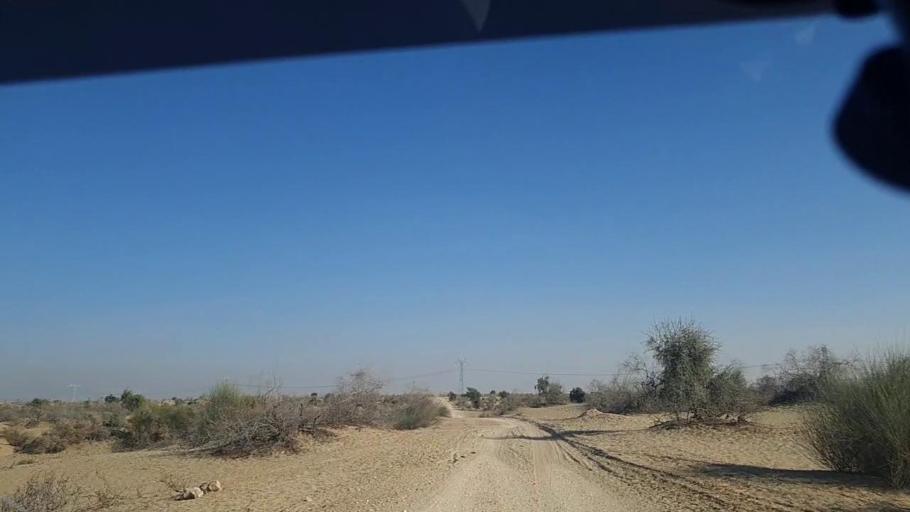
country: PK
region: Sindh
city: Khanpur
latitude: 27.6470
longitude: 69.3963
